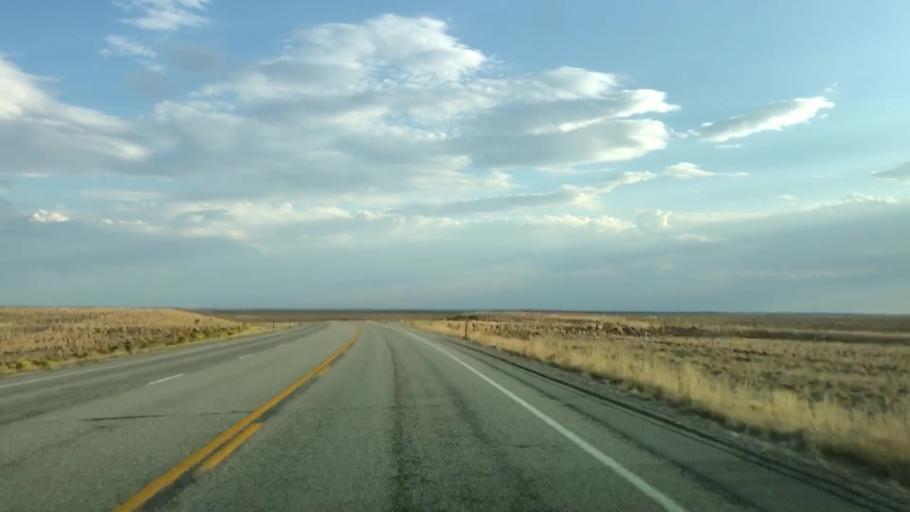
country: US
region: Wyoming
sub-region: Sweetwater County
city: North Rock Springs
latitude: 42.1944
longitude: -109.4807
